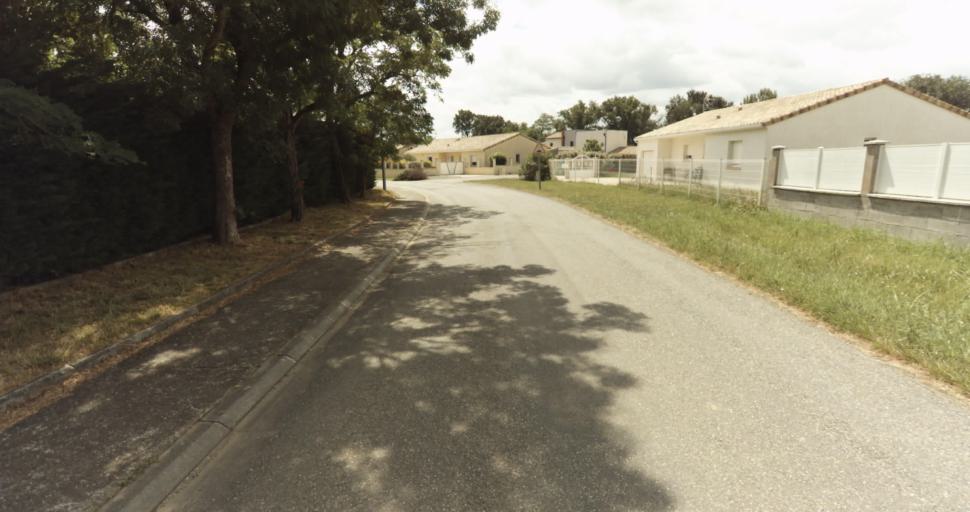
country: FR
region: Midi-Pyrenees
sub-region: Departement de la Haute-Garonne
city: Fontenilles
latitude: 43.5564
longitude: 1.1834
